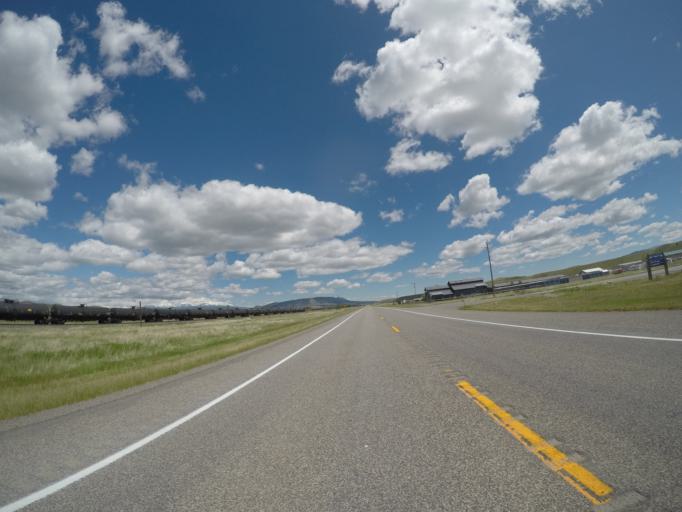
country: US
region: Montana
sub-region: Park County
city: Livingston
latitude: 45.6831
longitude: -110.5160
